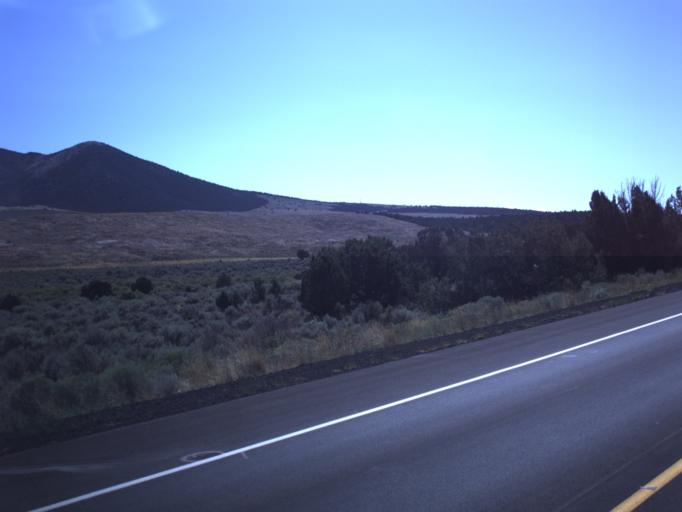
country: US
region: Utah
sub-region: Utah County
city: Eagle Mountain
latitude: 40.0123
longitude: -112.2771
